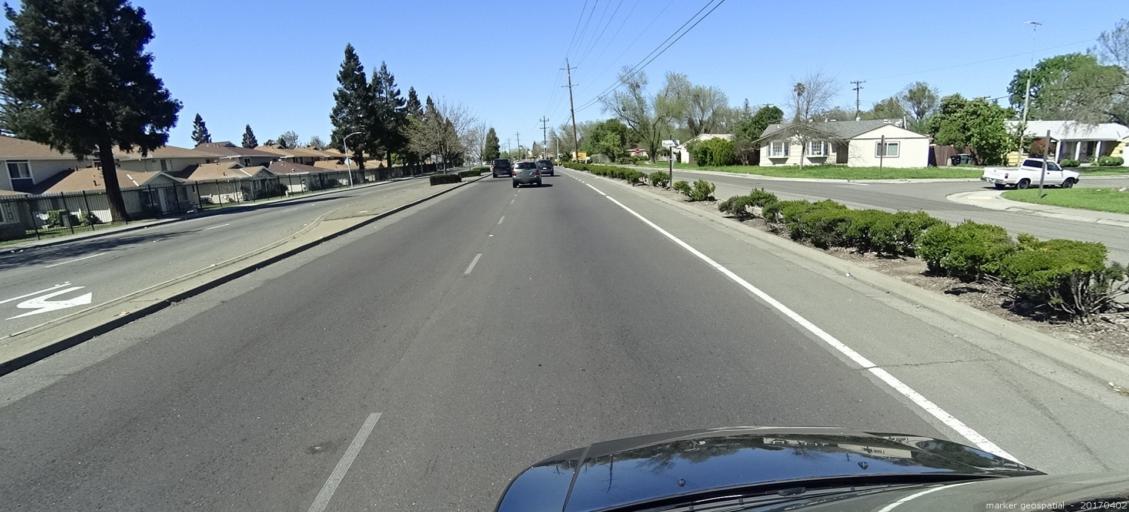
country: US
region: California
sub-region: Sacramento County
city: Parkway
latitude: 38.4879
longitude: -121.4551
